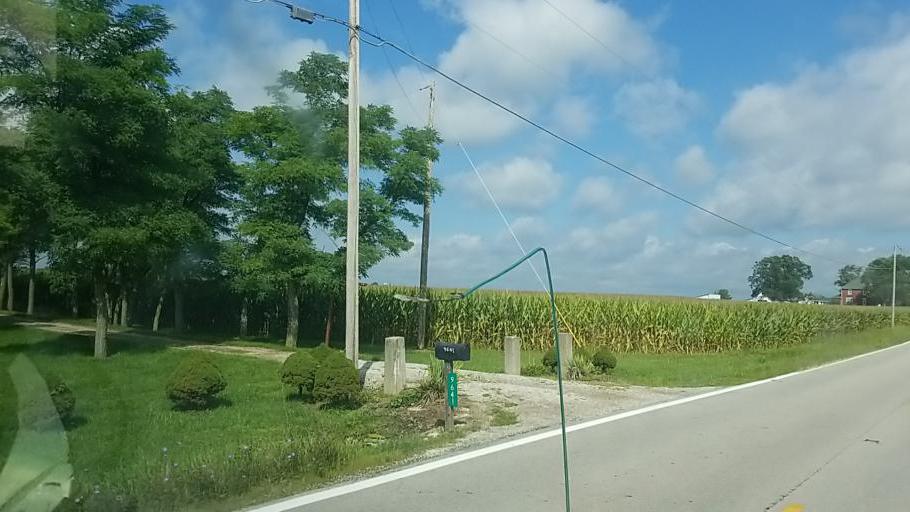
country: US
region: Ohio
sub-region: Pickaway County
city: Commercial Point
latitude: 39.7880
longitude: -83.1217
